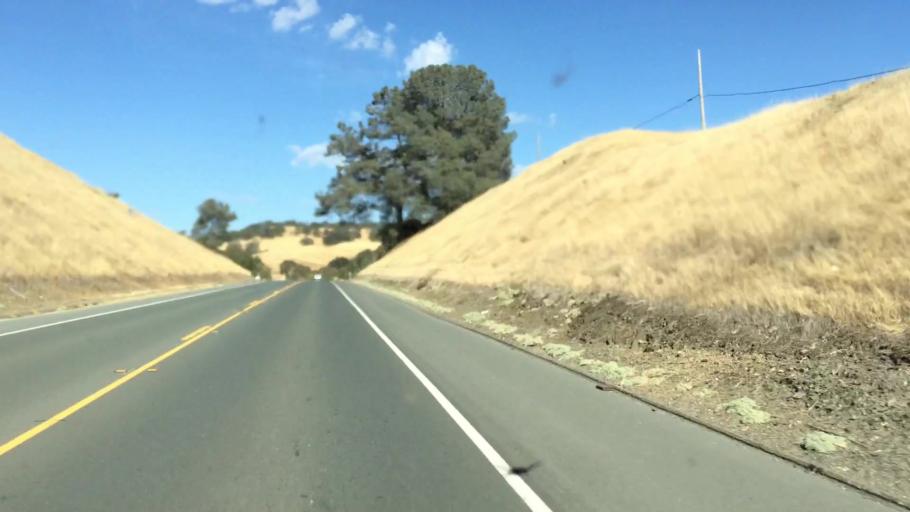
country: US
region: California
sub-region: Amador County
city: Ione
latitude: 38.3661
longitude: -120.9237
